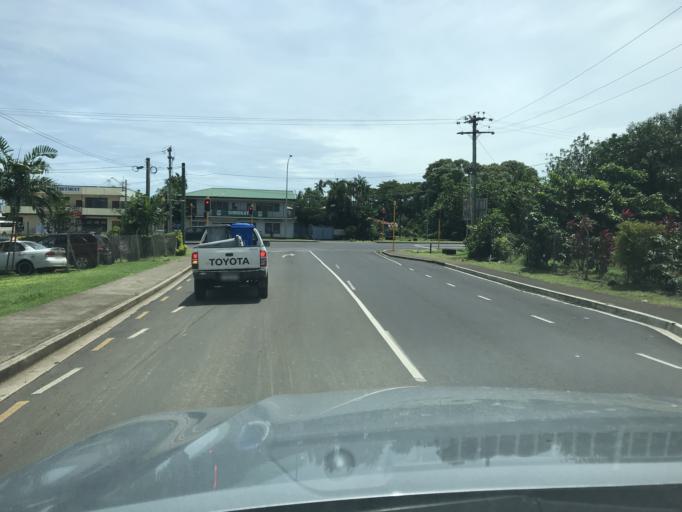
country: WS
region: Tuamasaga
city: Vaiusu
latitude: -13.8231
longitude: -171.8004
